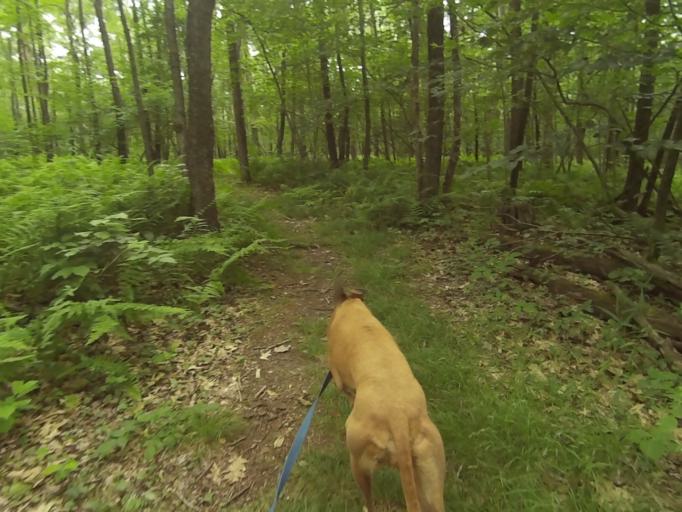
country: US
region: Pennsylvania
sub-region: Centre County
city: Stormstown
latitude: 40.9183
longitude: -78.0701
